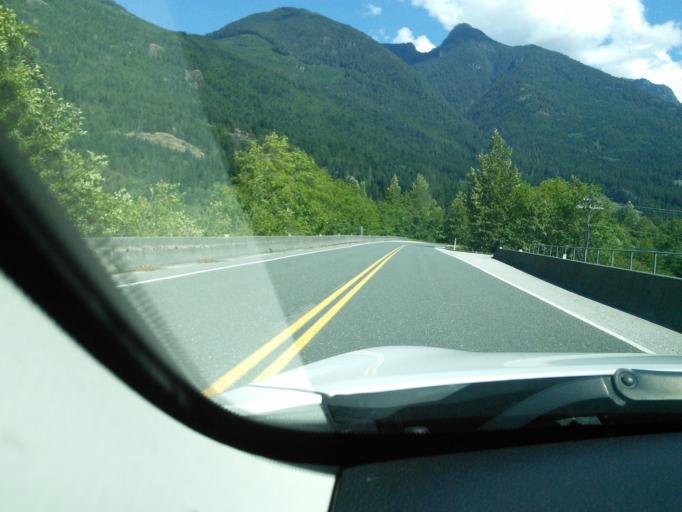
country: CA
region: British Columbia
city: Campbell River
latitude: 50.3610
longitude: -125.9169
